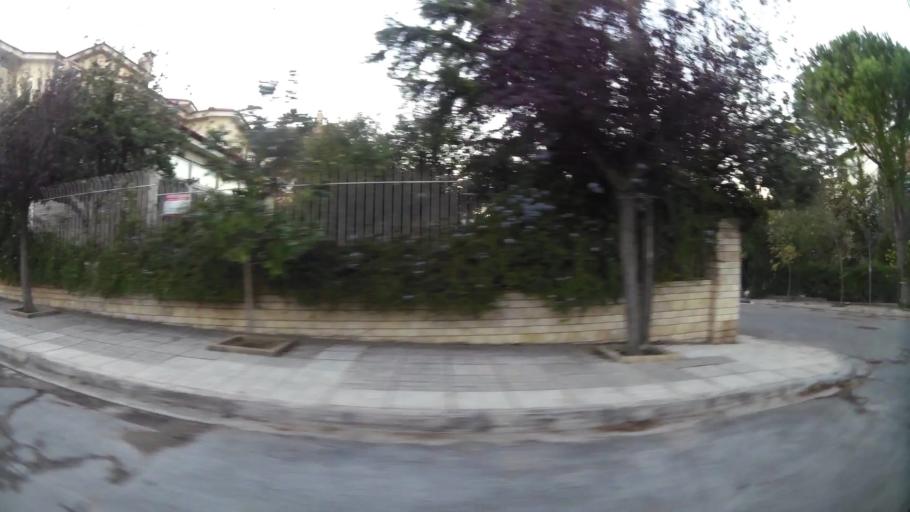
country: GR
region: Attica
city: Pefki
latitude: 38.0634
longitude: 23.7886
